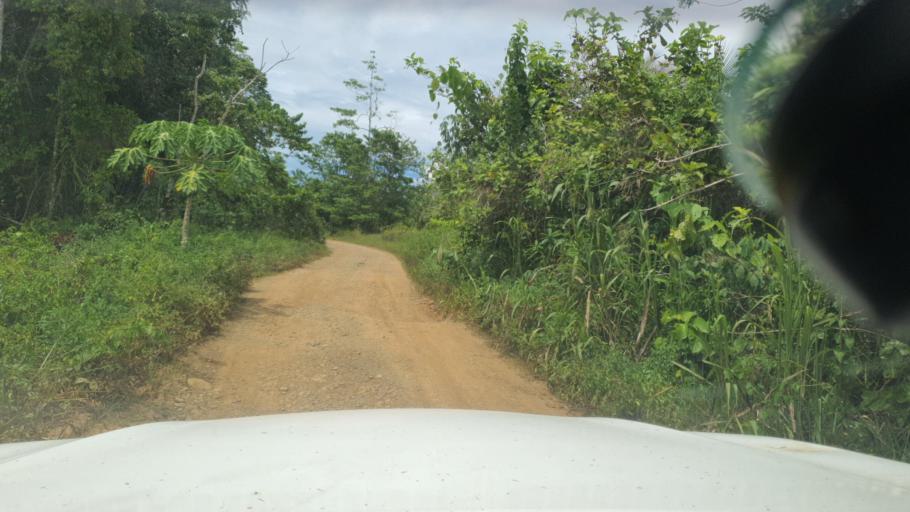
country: SB
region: Guadalcanal
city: Honiara
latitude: -9.4848
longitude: 160.3232
